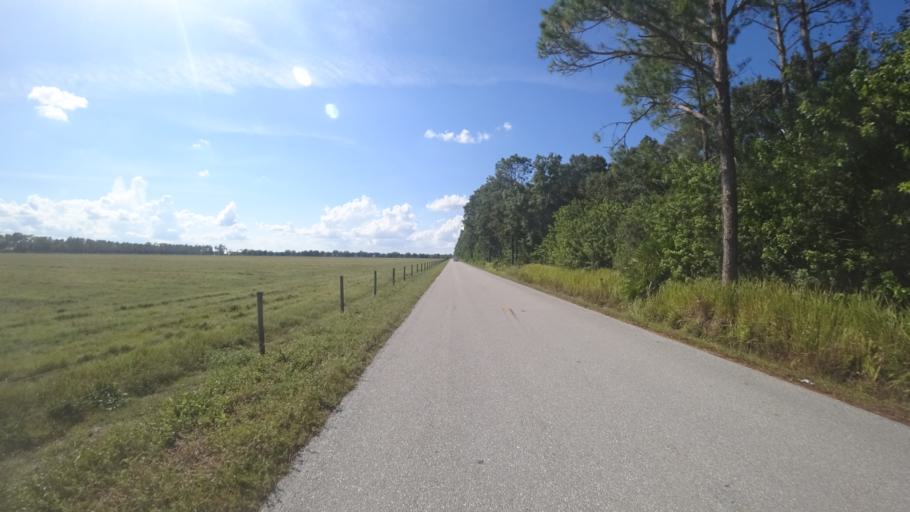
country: US
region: Florida
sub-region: Sarasota County
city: The Meadows
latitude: 27.4308
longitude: -82.2972
